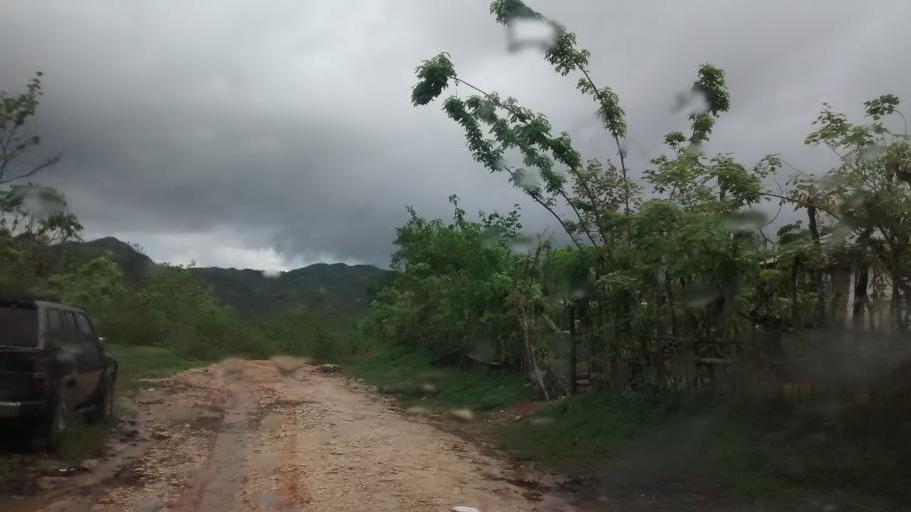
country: HT
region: Grandans
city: Corail
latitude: 18.5362
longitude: -73.9910
